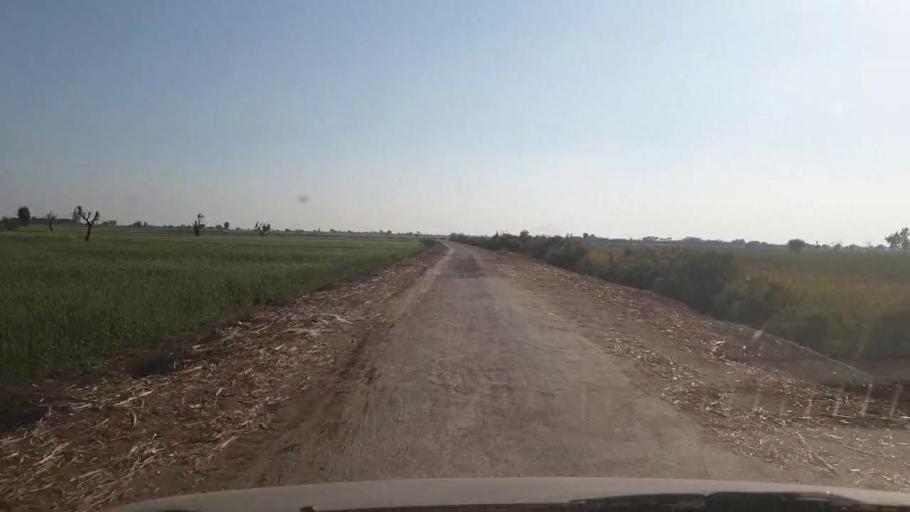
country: PK
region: Sindh
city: Mirwah Gorchani
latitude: 25.3640
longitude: 69.0957
